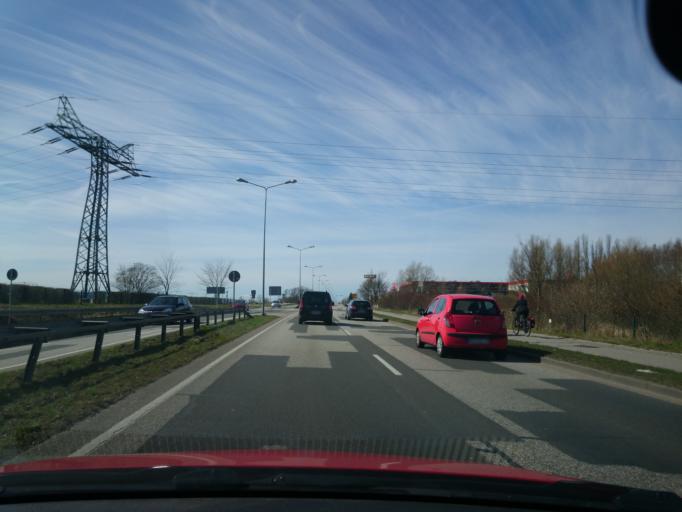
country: DE
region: Mecklenburg-Vorpommern
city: Lambrechtshagen
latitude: 54.1053
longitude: 12.0626
